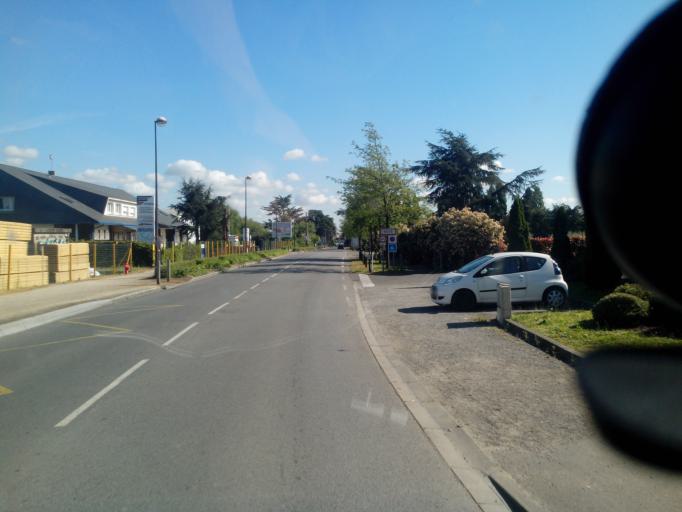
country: FR
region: Pays de la Loire
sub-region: Departement de la Loire-Atlantique
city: Bouguenais
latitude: 47.1890
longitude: -1.5870
